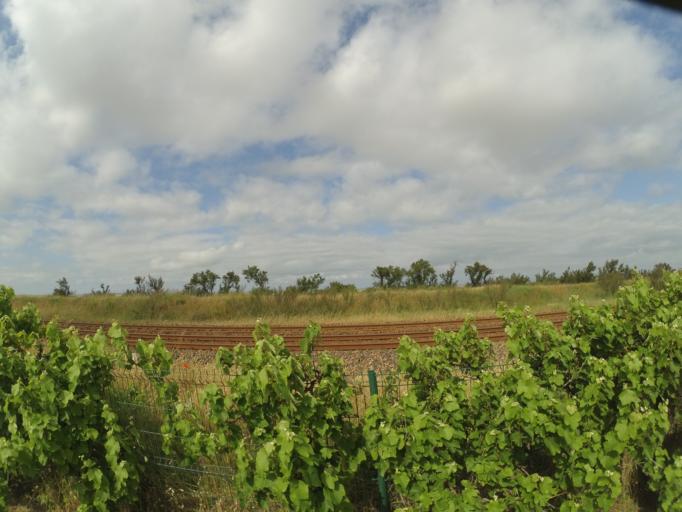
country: FR
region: Poitou-Charentes
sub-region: Departement de la Charente-Maritime
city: Angoulins
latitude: 46.0909
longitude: -1.0990
